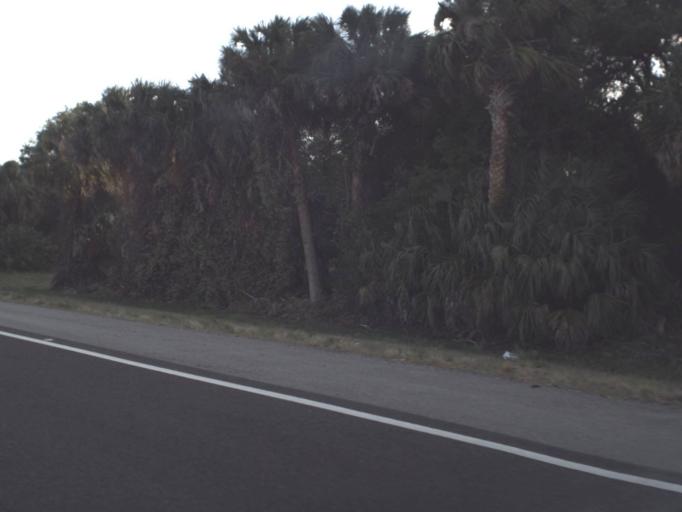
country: US
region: Florida
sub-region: Brevard County
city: Port Saint John
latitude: 28.4456
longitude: -80.8210
